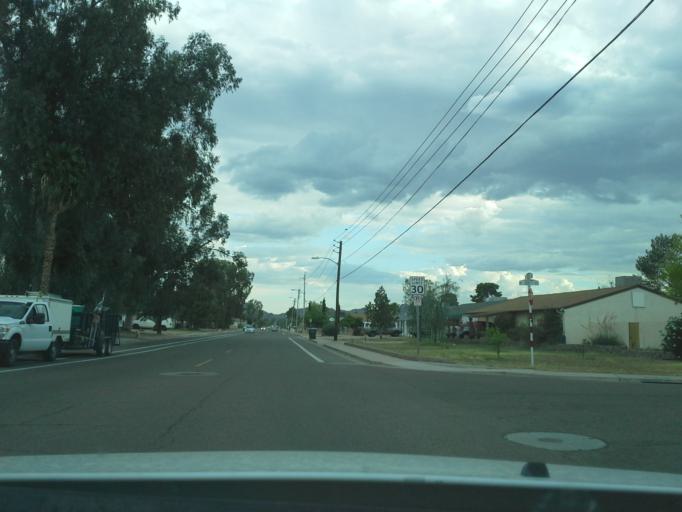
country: US
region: Arizona
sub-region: Maricopa County
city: Paradise Valley
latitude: 33.6103
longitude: -112.0047
